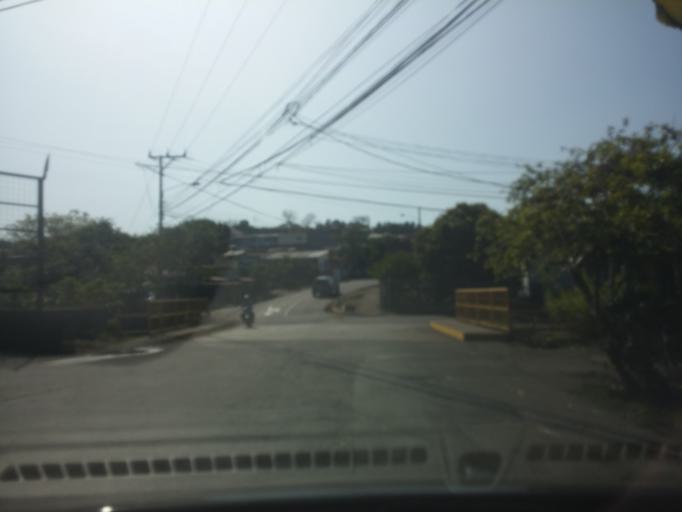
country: CR
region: Heredia
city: Mercedes
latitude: 10.0099
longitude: -84.1344
